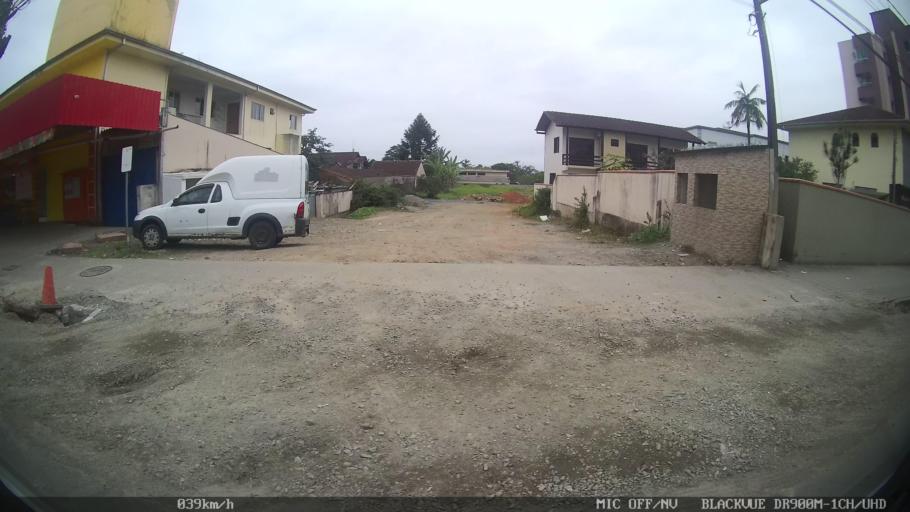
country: BR
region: Santa Catarina
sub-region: Joinville
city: Joinville
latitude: -26.3038
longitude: -48.8270
